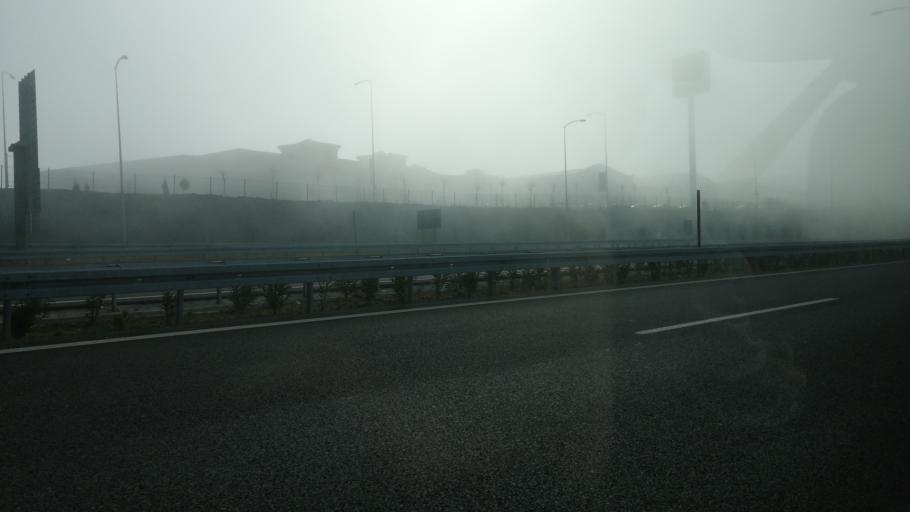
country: TR
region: Kocaeli
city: Tavsanli
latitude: 40.7745
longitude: 29.5184
